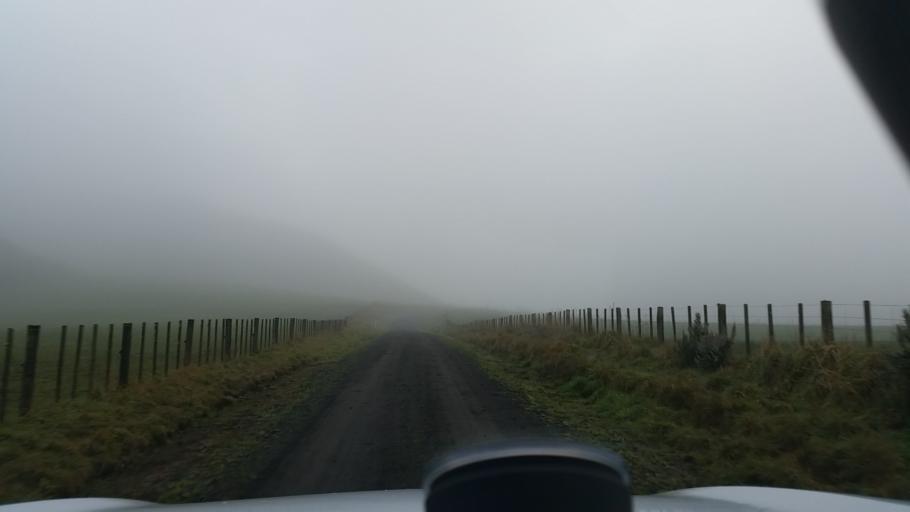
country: NZ
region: Taranaki
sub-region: South Taranaki District
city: Eltham
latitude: -39.4208
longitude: 174.4367
